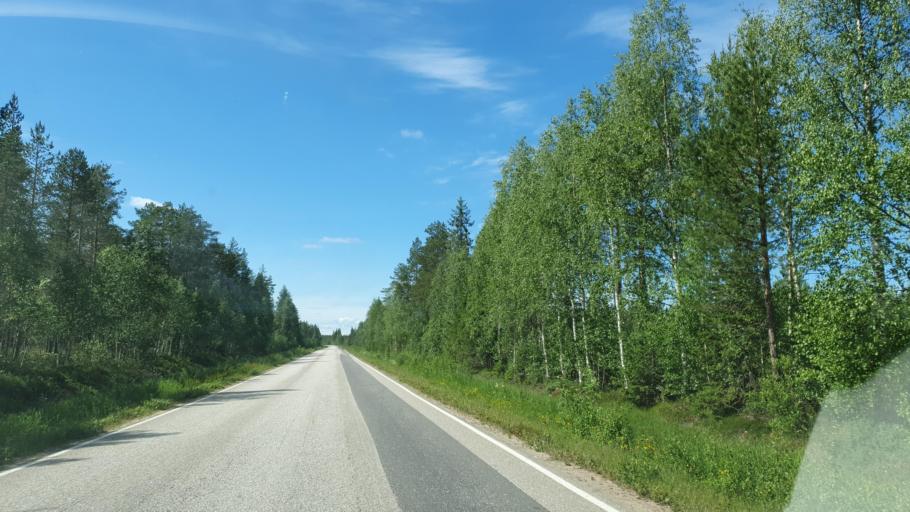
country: FI
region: Kainuu
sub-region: Kehys-Kainuu
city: Suomussalmi
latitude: 64.5727
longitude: 29.0015
